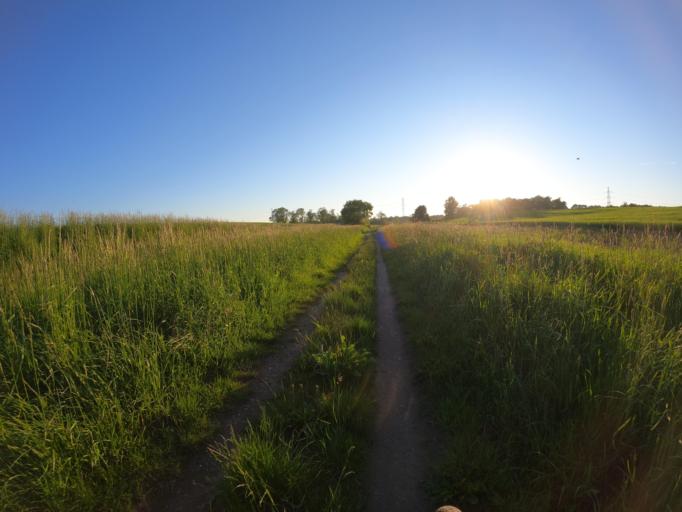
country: DK
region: Zealand
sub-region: Greve Kommune
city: Tune
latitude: 55.6261
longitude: 12.2311
